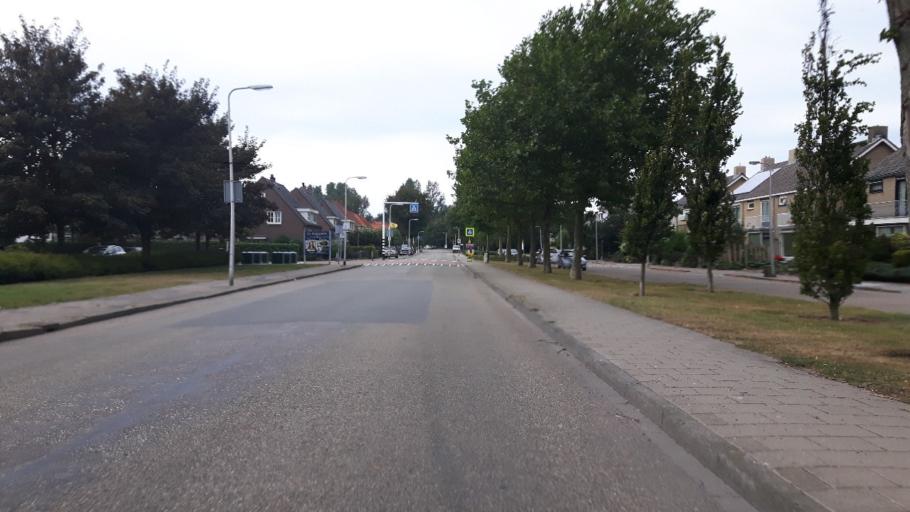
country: NL
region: South Holland
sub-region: Gemeente Hillegom
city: Hillegom
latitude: 52.3027
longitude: 4.5443
